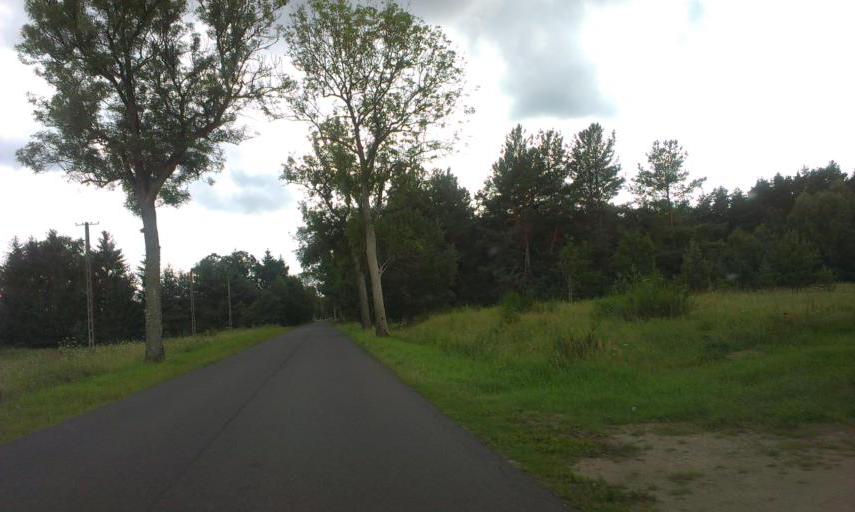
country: PL
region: West Pomeranian Voivodeship
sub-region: Powiat bialogardzki
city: Tychowo
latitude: 53.8619
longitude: 16.1654
